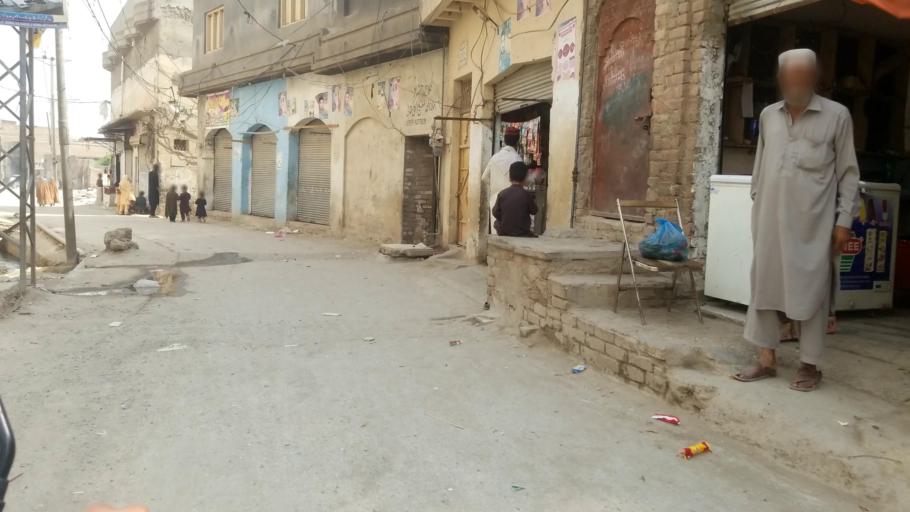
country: PK
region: Khyber Pakhtunkhwa
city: Peshawar
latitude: 33.9878
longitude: 71.5415
